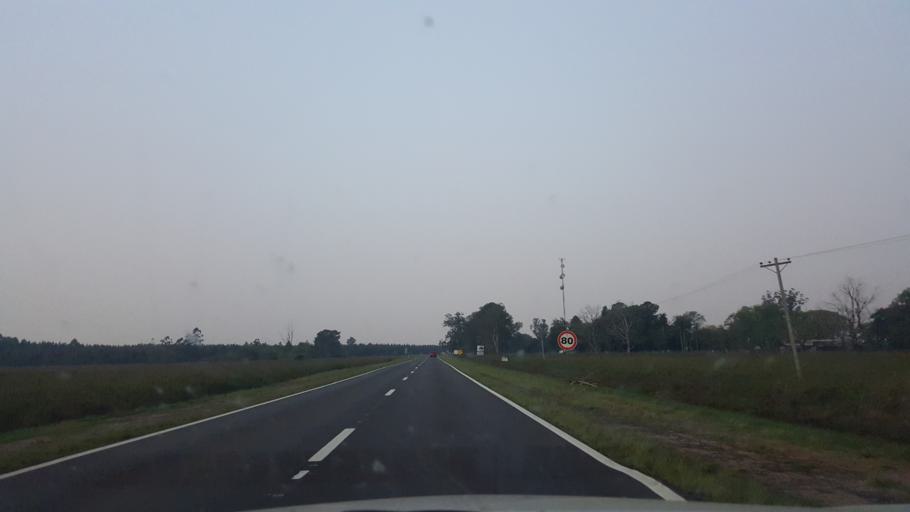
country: PY
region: Misiones
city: Ayolas
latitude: -27.6262
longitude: -56.9201
